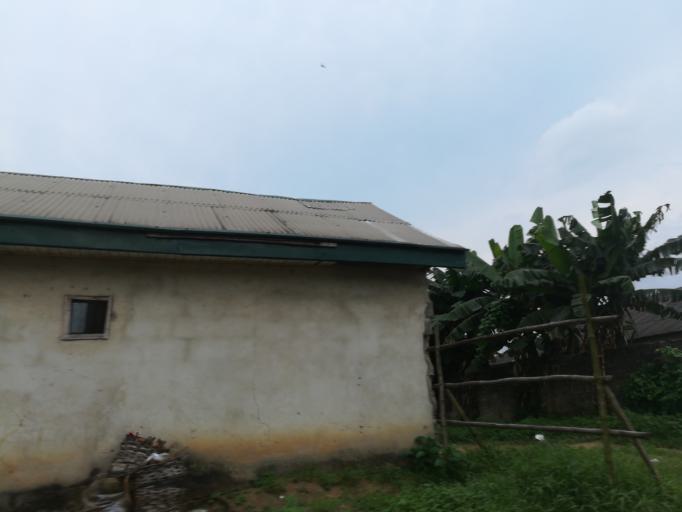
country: NG
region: Rivers
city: Okrika
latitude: 4.7817
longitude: 7.1290
